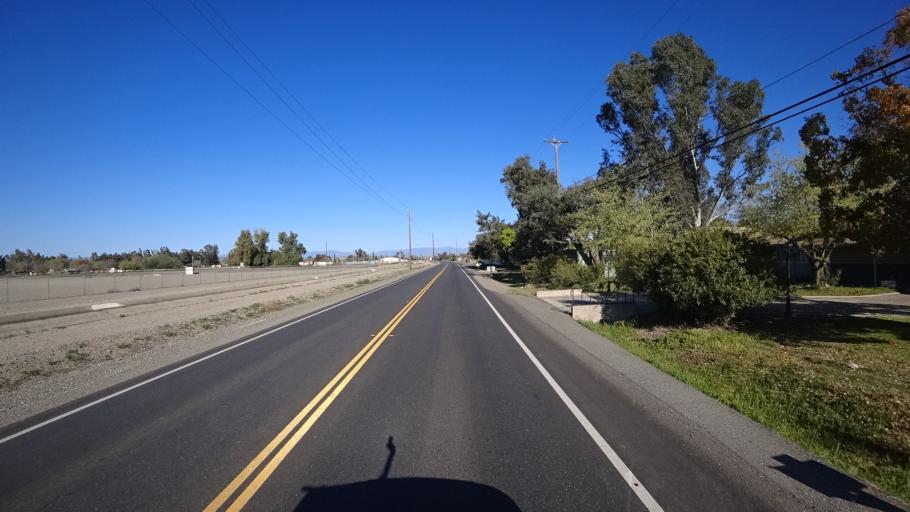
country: US
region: California
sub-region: Glenn County
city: Orland
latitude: 39.7580
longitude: -122.2231
